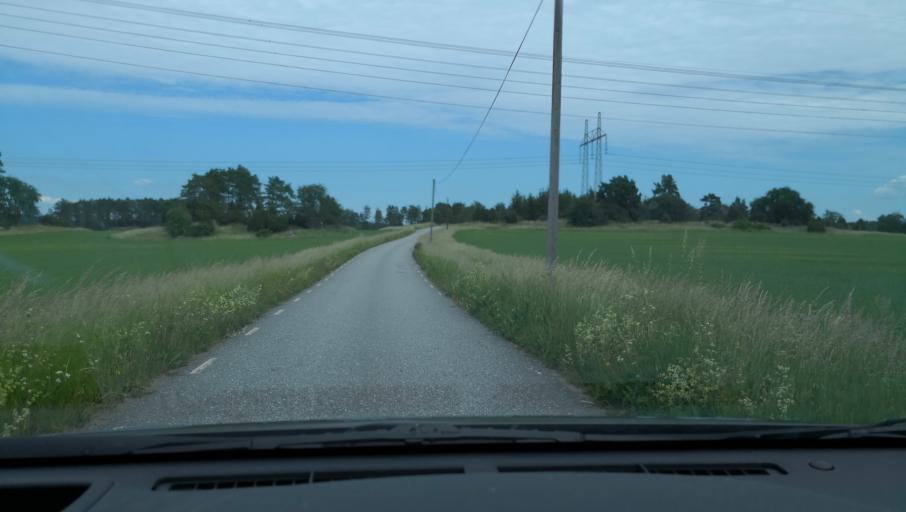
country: SE
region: Uppsala
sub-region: Enkopings Kommun
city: Orsundsbro
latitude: 59.6900
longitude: 17.3837
